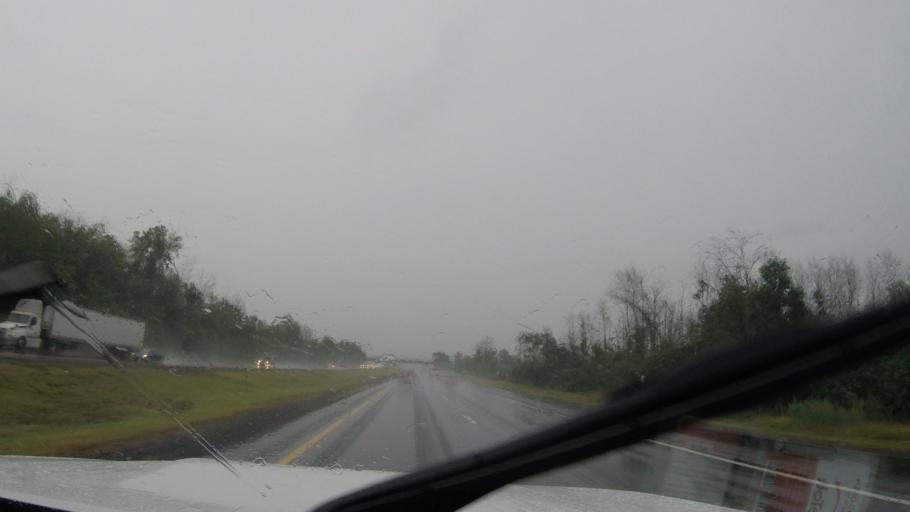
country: US
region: New York
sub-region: Seneca County
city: Waterloo
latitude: 42.9653
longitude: -76.8702
